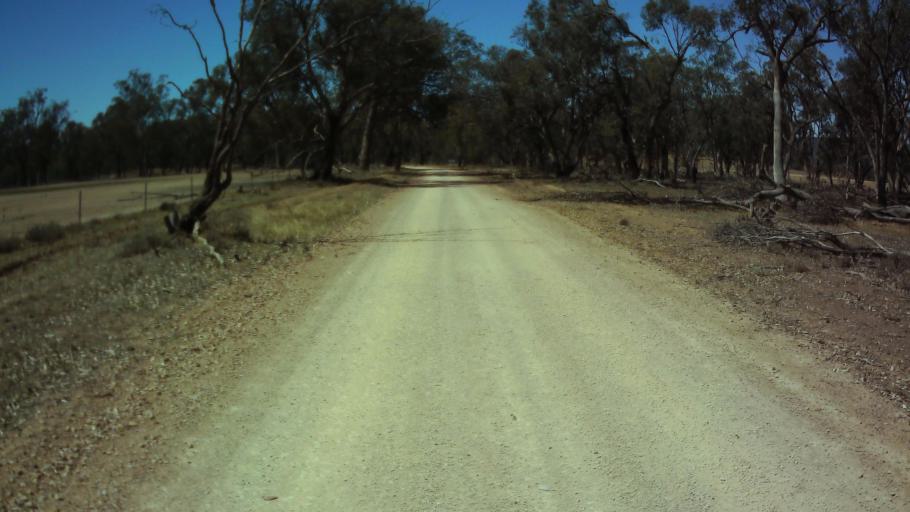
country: AU
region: New South Wales
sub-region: Weddin
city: Grenfell
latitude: -33.9359
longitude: 148.0774
